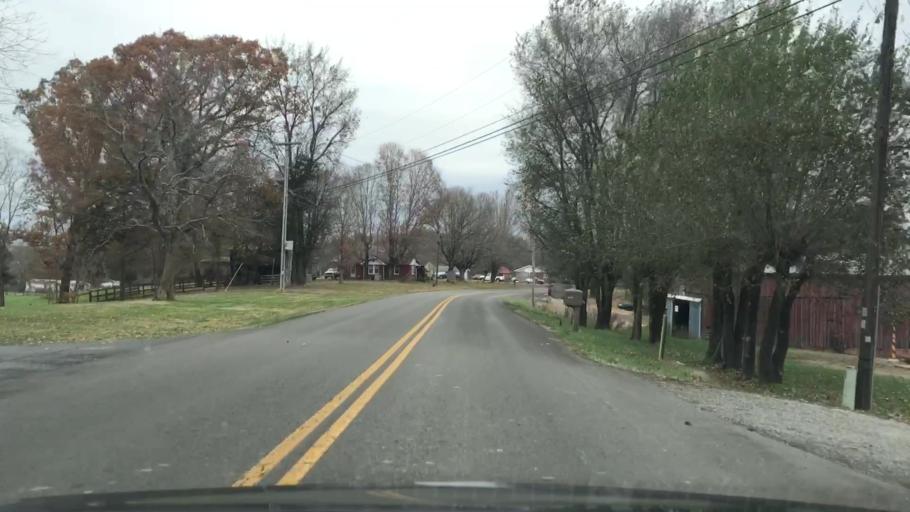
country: US
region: Kentucky
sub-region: Metcalfe County
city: Edmonton
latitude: 36.9501
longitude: -85.6147
